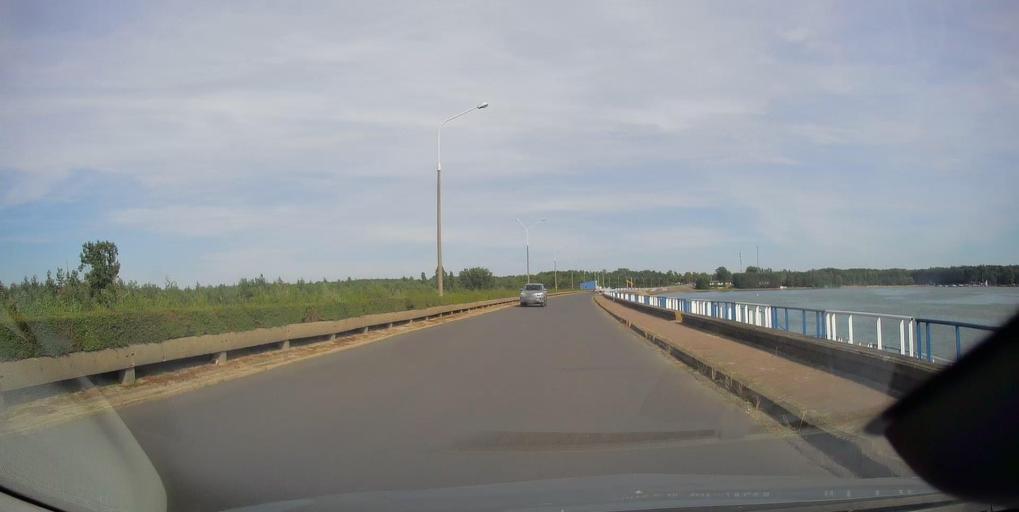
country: PL
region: Lodz Voivodeship
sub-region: Powiat tomaszowski
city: Tomaszow Mazowiecki
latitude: 51.4746
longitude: 19.9998
